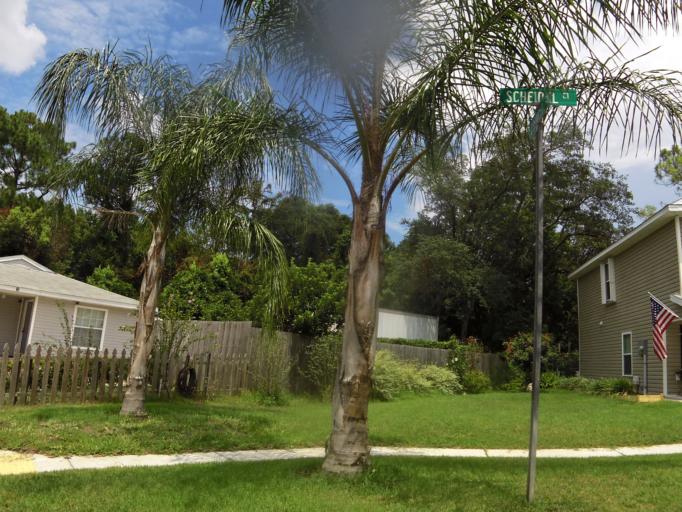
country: US
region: Florida
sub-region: Duval County
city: Atlantic Beach
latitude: 30.3274
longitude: -81.4160
